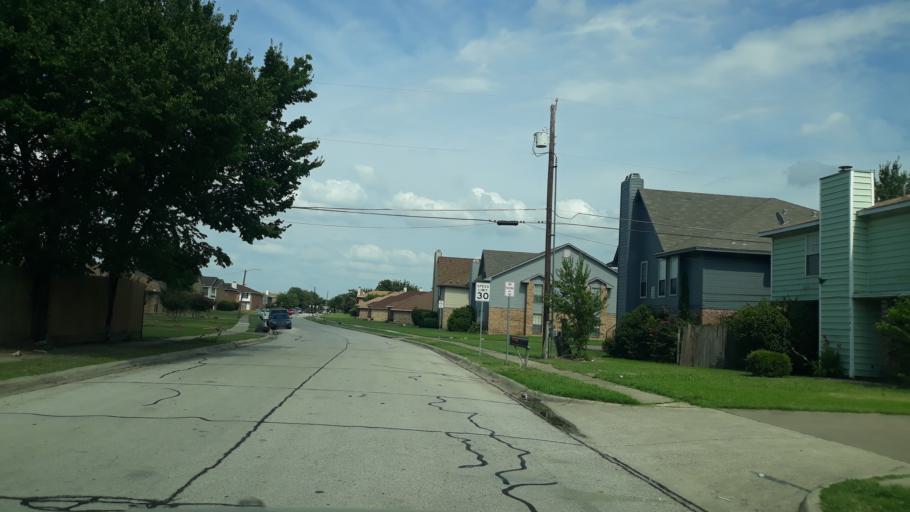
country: US
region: Texas
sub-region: Dallas County
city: Irving
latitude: 32.8136
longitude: -96.9898
